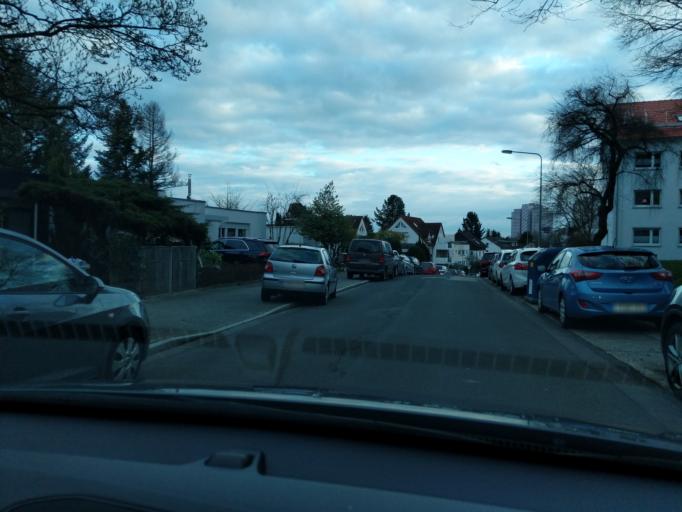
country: DE
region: Hesse
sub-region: Regierungsbezirk Darmstadt
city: Bad Vilbel
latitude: 50.1462
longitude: 8.7211
